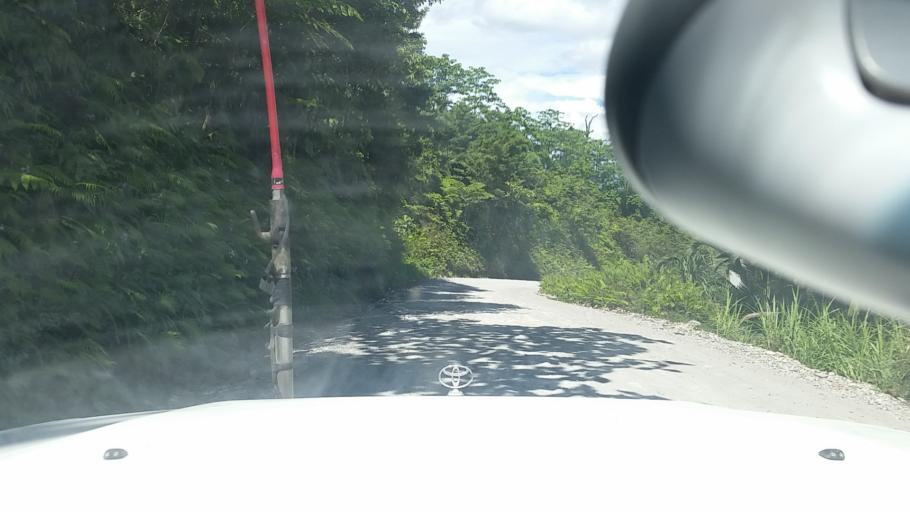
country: PG
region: Western Province
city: Kiunga
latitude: -5.5534
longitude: 141.2678
